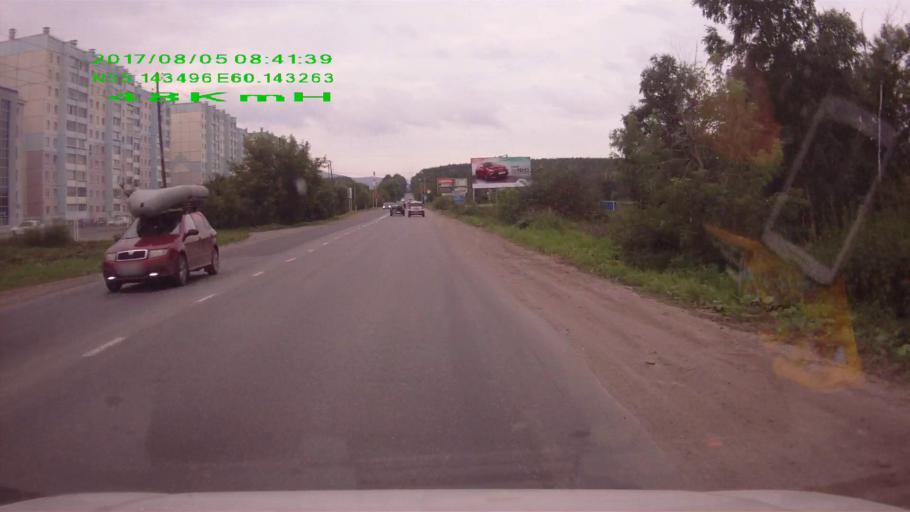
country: RU
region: Chelyabinsk
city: Turgoyak
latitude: 55.1432
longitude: 60.1433
